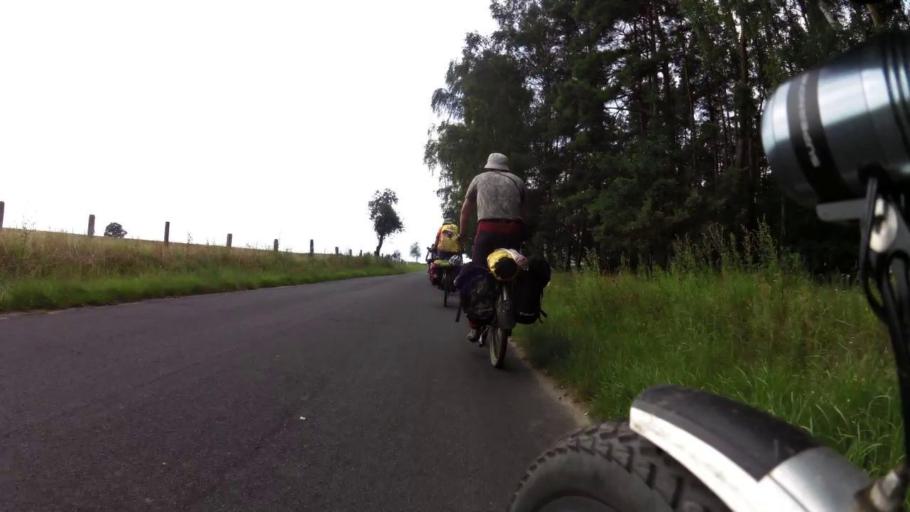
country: PL
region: West Pomeranian Voivodeship
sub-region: Powiat mysliborski
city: Debno
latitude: 52.7896
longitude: 14.6657
